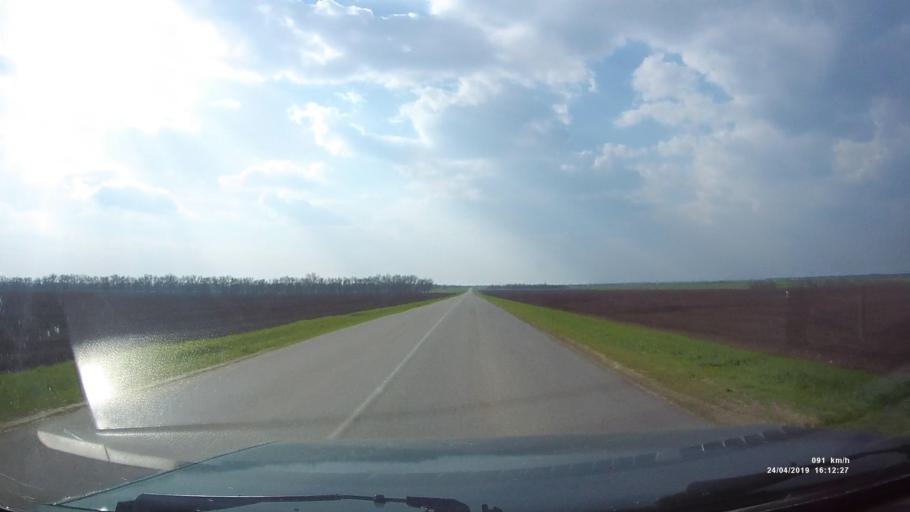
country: RU
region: Rostov
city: Sovetskoye
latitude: 46.7329
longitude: 42.2372
